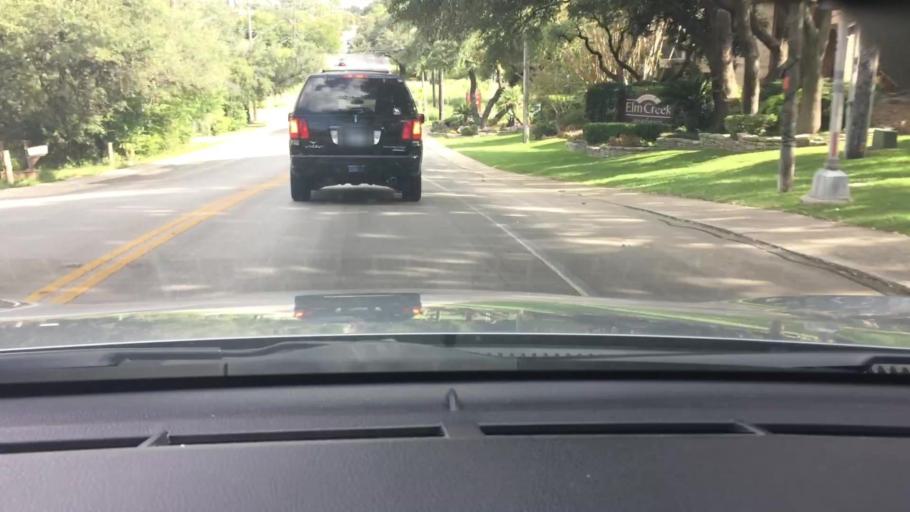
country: US
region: Texas
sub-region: Bexar County
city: Shavano Park
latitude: 29.5496
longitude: -98.5679
